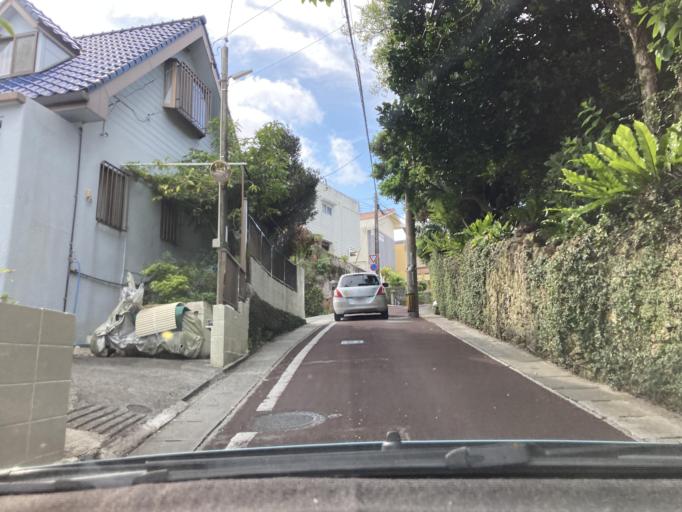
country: JP
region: Okinawa
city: Naha-shi
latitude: 26.2221
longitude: 127.7180
